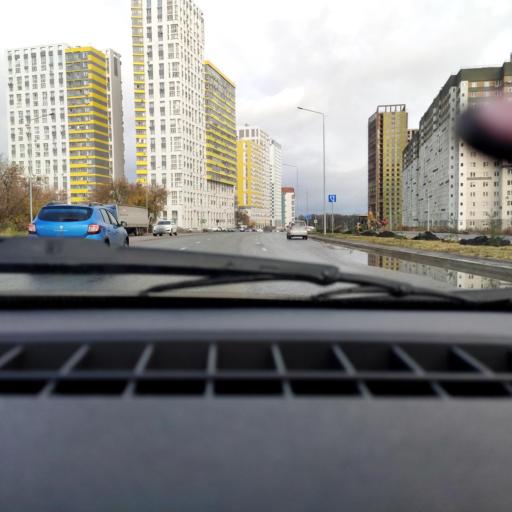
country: RU
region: Bashkortostan
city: Ufa
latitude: 54.7614
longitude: 56.0306
